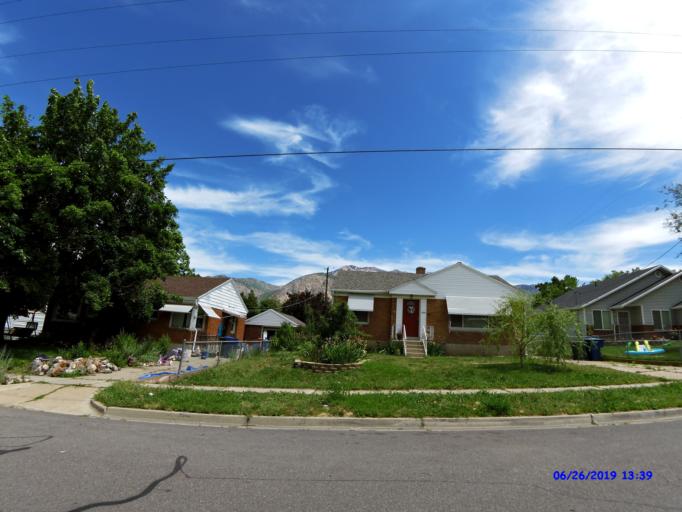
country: US
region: Utah
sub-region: Weber County
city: South Ogden
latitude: 41.2024
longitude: -111.9653
